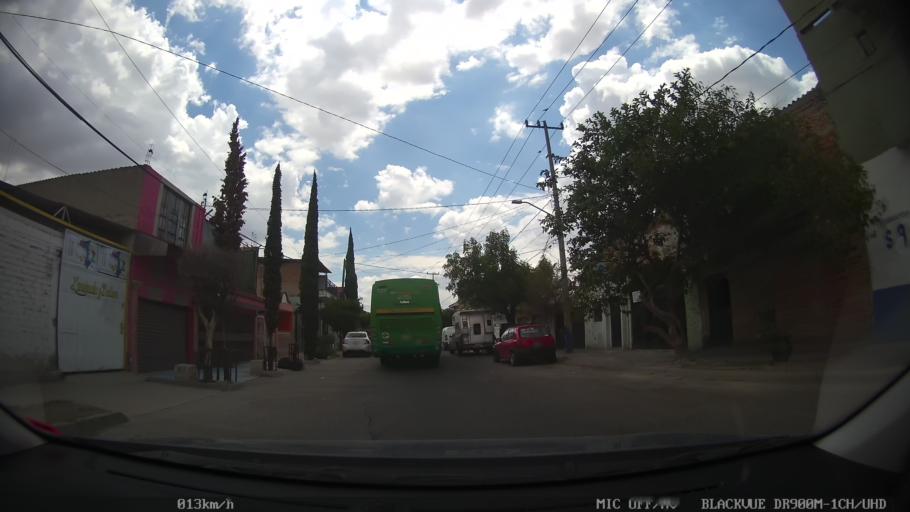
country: MX
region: Jalisco
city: Tlaquepaque
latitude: 20.6531
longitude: -103.2800
